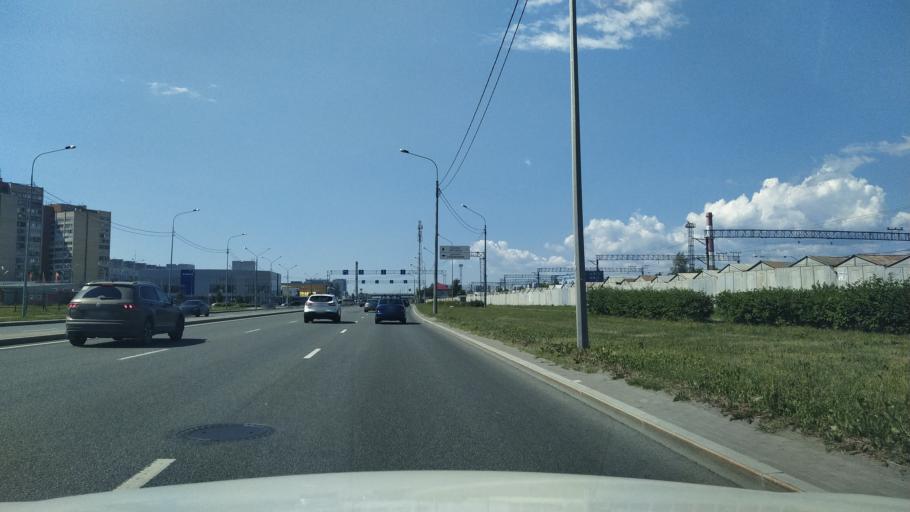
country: RU
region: Leningrad
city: Parnas
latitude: 60.0560
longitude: 30.3642
